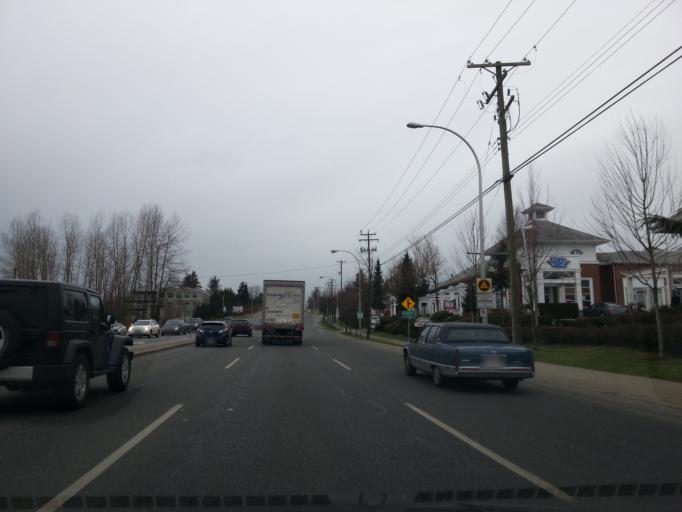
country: CA
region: British Columbia
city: Surrey
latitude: 49.1046
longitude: -122.8028
